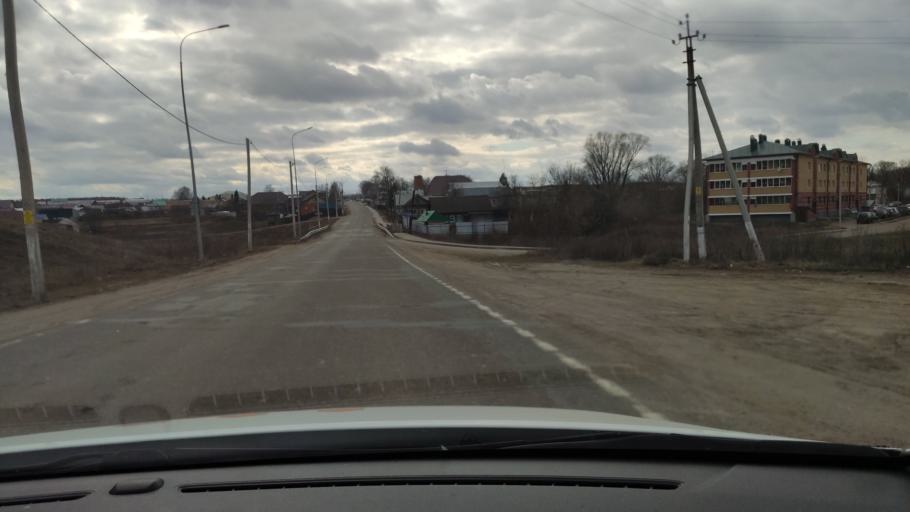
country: RU
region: Tatarstan
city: Vysokaya Gora
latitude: 56.1246
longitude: 49.1981
